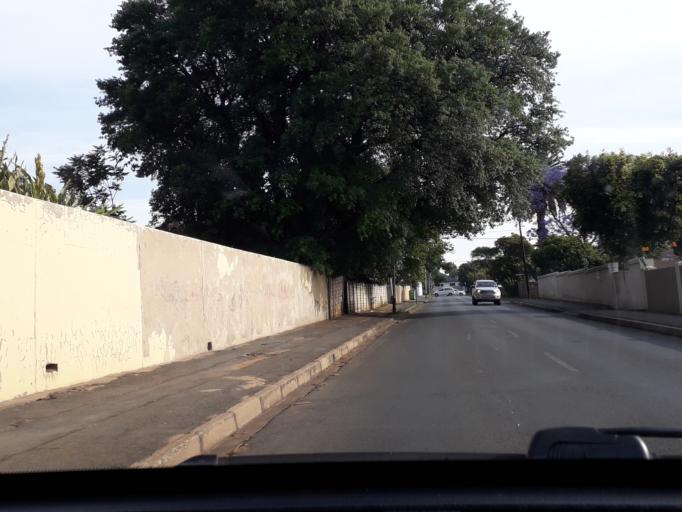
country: ZA
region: Gauteng
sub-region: City of Johannesburg Metropolitan Municipality
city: Johannesburg
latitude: -26.1513
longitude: 28.0968
